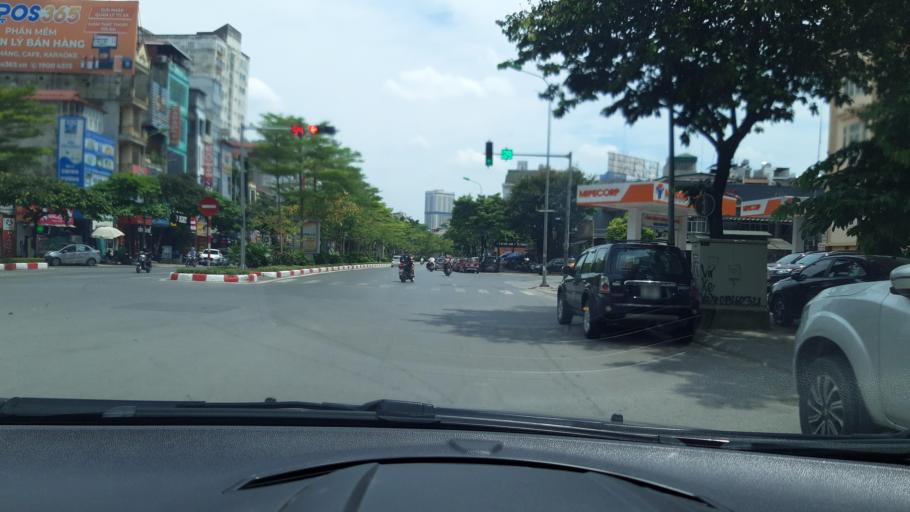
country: VN
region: Ha Noi
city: Cau Giay
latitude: 21.0403
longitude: 105.7903
